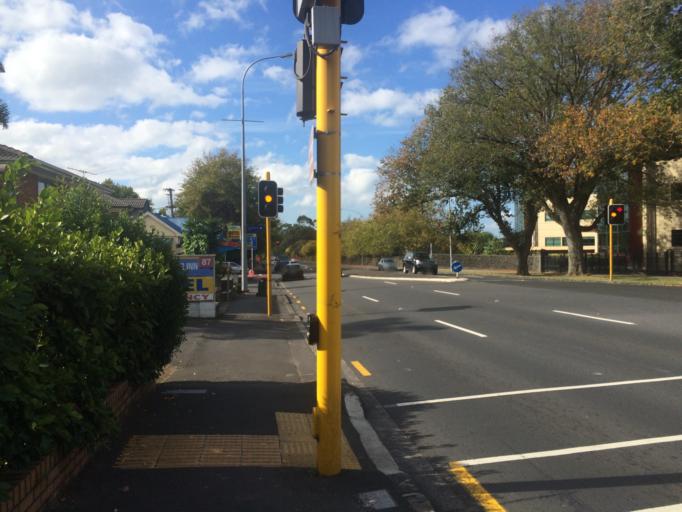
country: NZ
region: Auckland
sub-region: Auckland
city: Auckland
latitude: -36.8876
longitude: 174.7993
